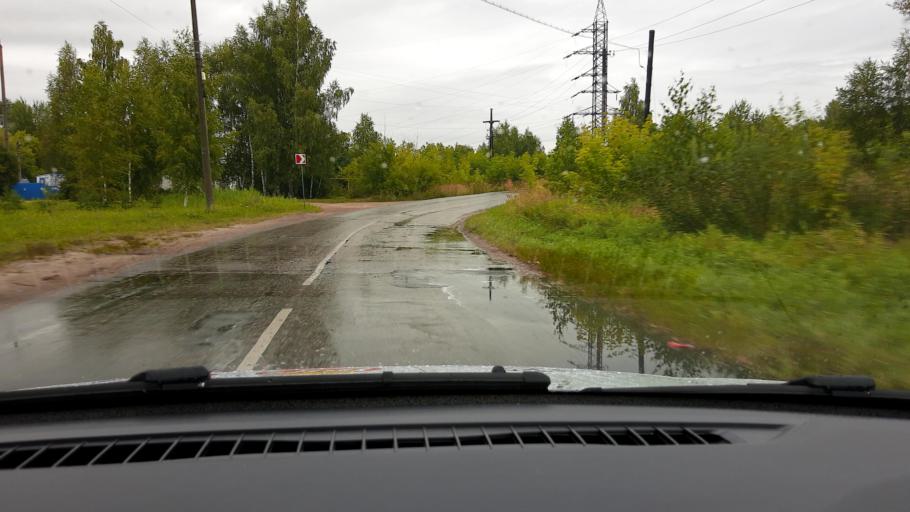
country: RU
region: Nizjnij Novgorod
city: Bogorodsk
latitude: 56.1127
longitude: 43.4832
